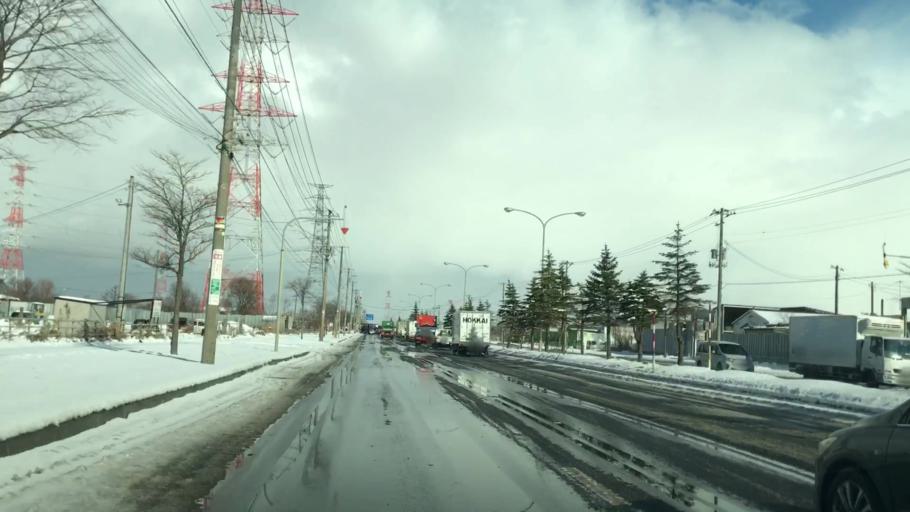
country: JP
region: Hokkaido
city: Sapporo
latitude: 43.1474
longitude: 141.4121
